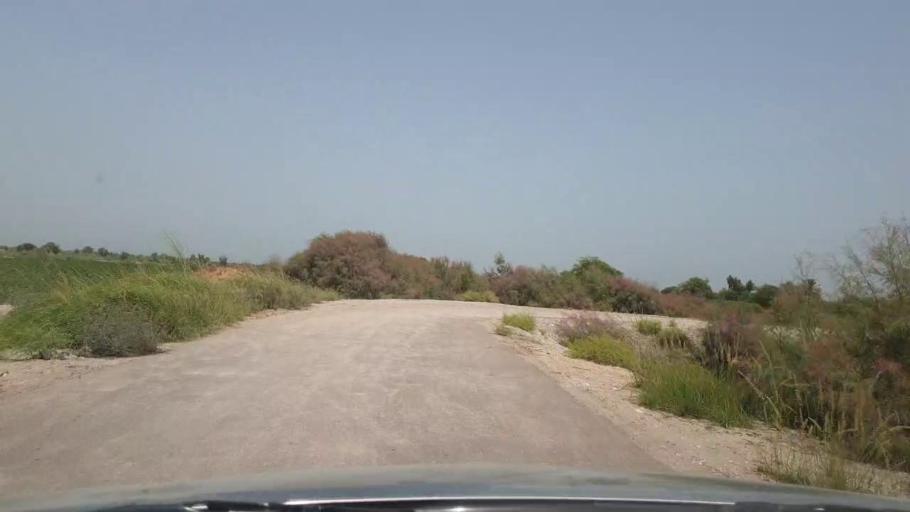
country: PK
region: Sindh
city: Pano Aqil
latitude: 27.8712
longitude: 69.1672
